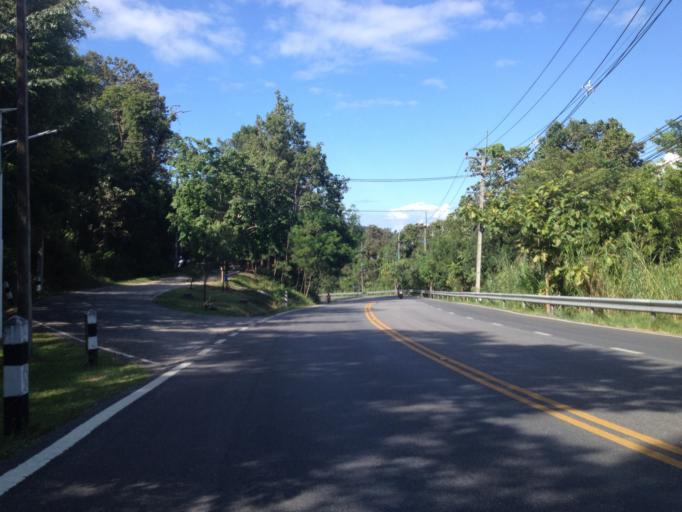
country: TH
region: Chiang Mai
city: Chiang Mai
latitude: 18.8081
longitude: 98.9376
